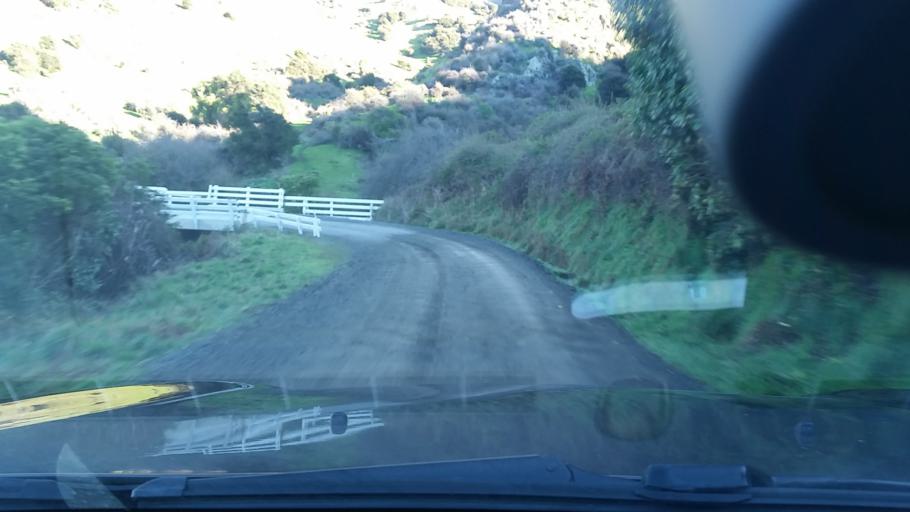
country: NZ
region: Marlborough
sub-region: Marlborough District
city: Blenheim
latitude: -41.6342
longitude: 173.9629
